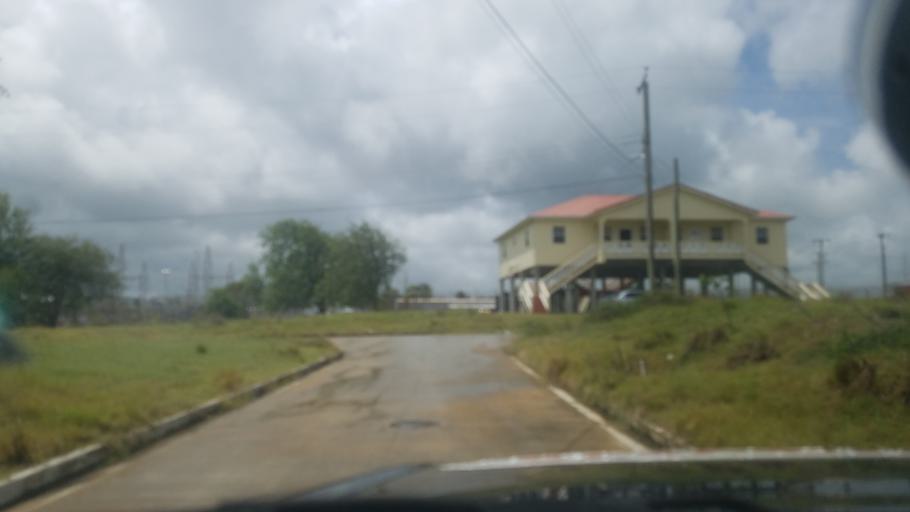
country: LC
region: Laborie Quarter
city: Laborie
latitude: 13.7509
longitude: -60.9762
